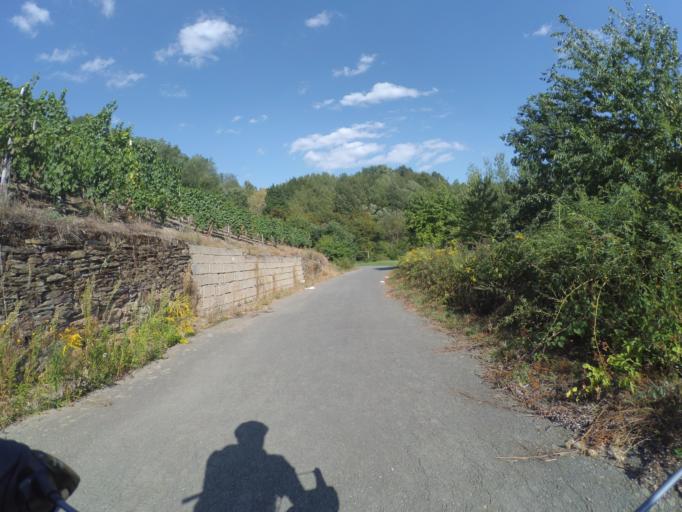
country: DE
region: Rheinland-Pfalz
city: Longuich
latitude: 49.8066
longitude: 6.7914
